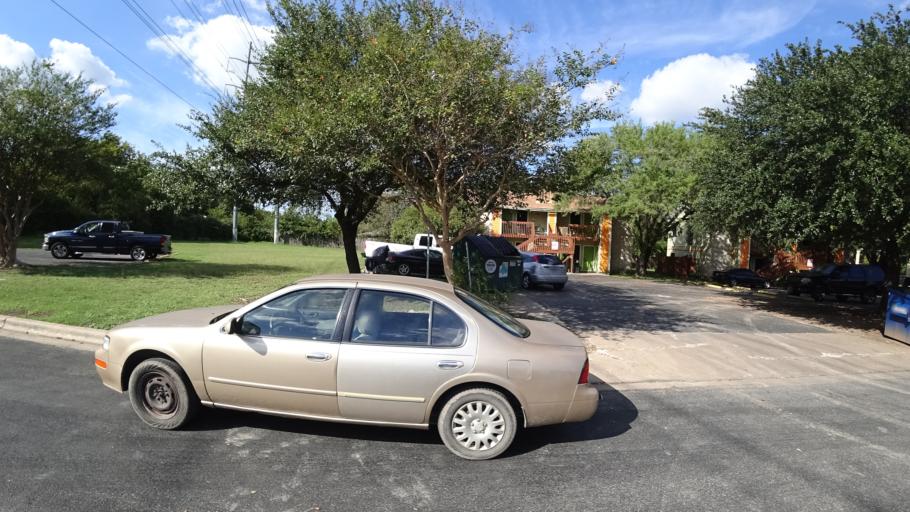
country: US
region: Texas
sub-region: Travis County
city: Rollingwood
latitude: 30.2069
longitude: -97.7871
